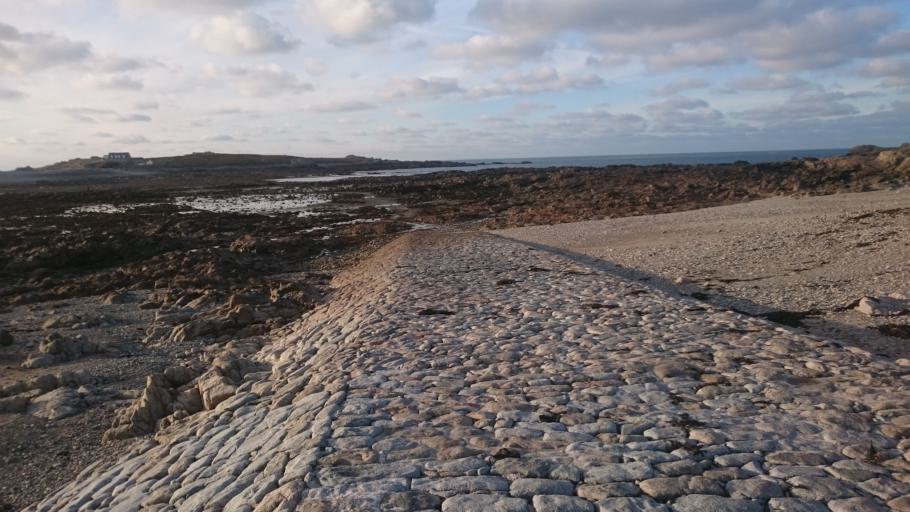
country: GG
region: St Peter Port
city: Saint Peter Port
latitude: 49.4573
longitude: -2.6578
